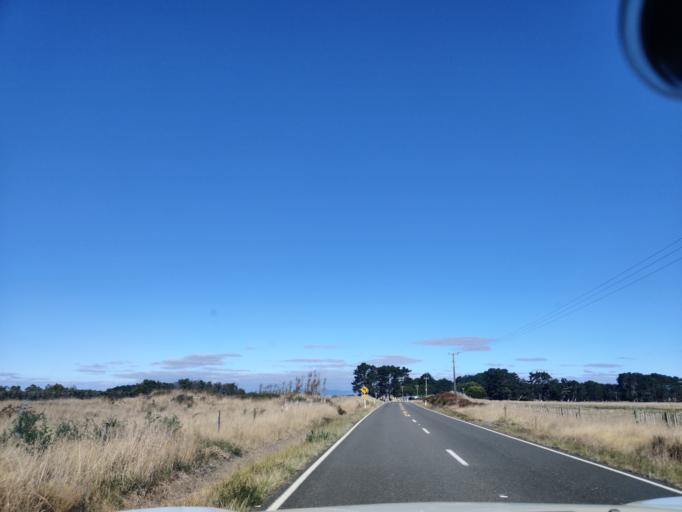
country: NZ
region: Manawatu-Wanganui
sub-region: Horowhenua District
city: Foxton
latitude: -40.3844
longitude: 175.2765
